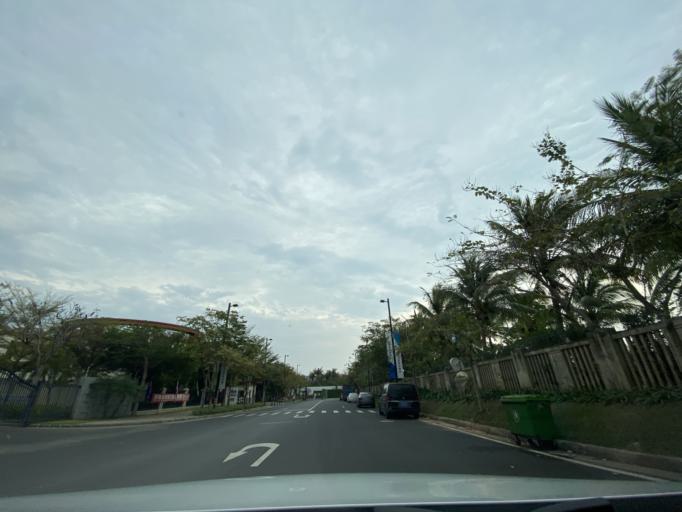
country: CN
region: Hainan
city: Yingzhou
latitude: 18.4038
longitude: 109.8564
